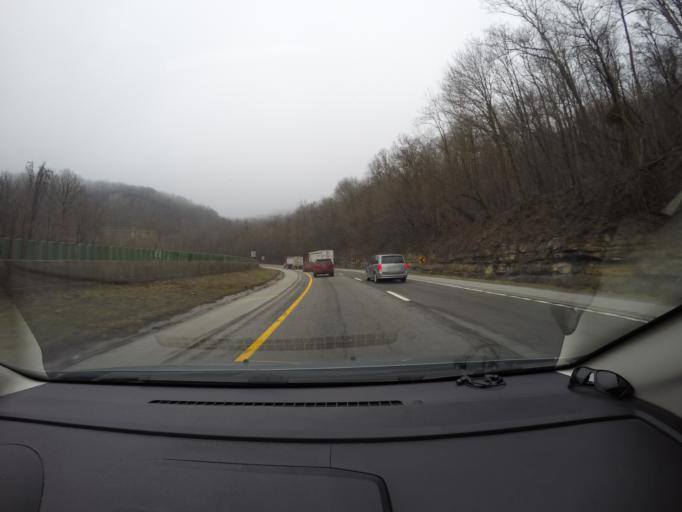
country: US
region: Tennessee
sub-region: Marion County
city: Monteagle
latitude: 35.2411
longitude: -85.8760
